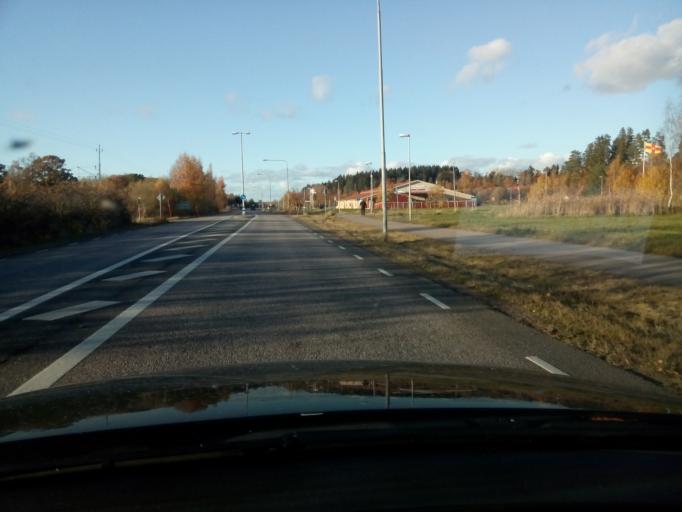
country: SE
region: Soedermanland
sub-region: Nykopings Kommun
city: Nykoping
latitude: 58.7277
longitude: 17.0131
